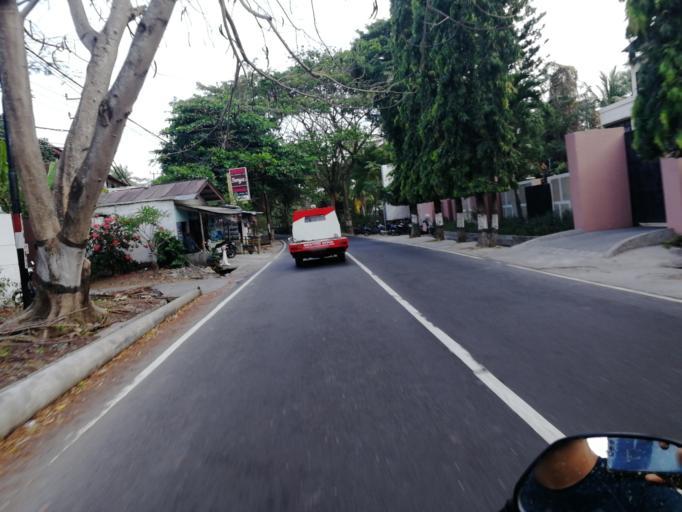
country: ID
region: West Nusa Tenggara
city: Karangsubagan
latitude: -8.4724
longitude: 116.0381
